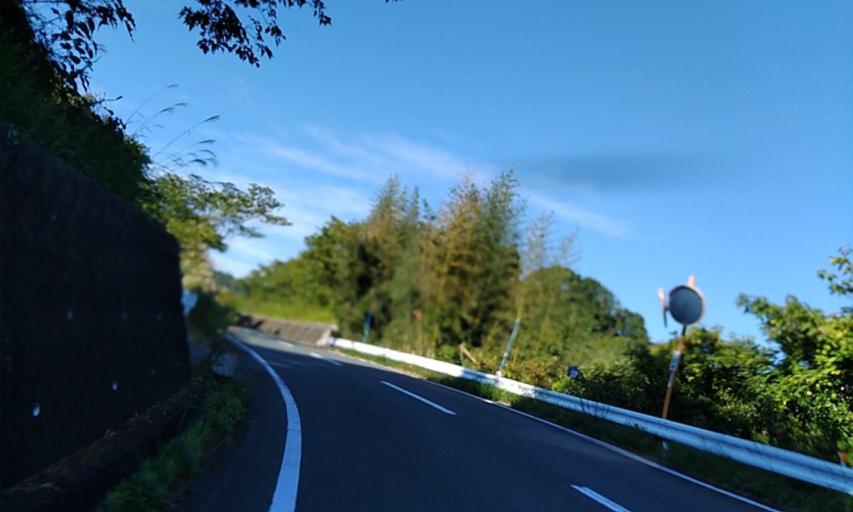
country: JP
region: Shizuoka
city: Hamakita
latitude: 34.8213
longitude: 137.6497
